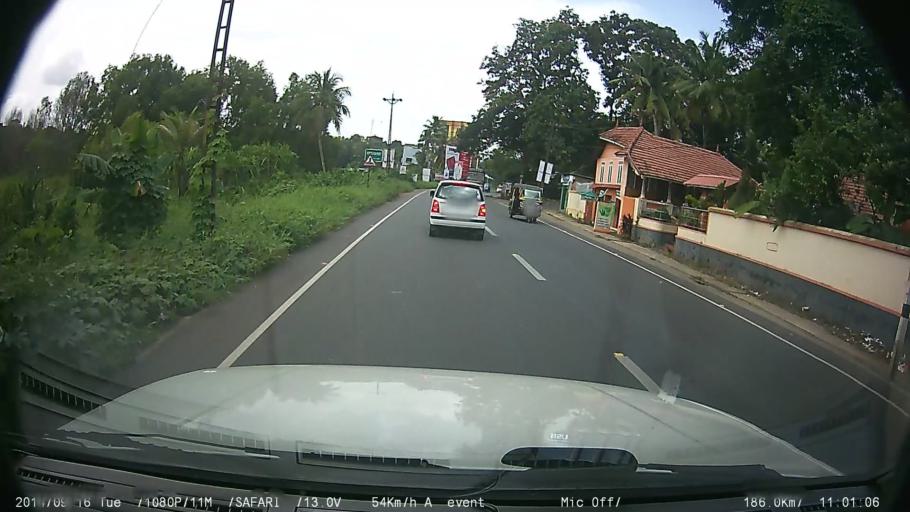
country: IN
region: Kerala
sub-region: Kottayam
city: Kottayam
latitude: 9.5590
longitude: 76.5153
